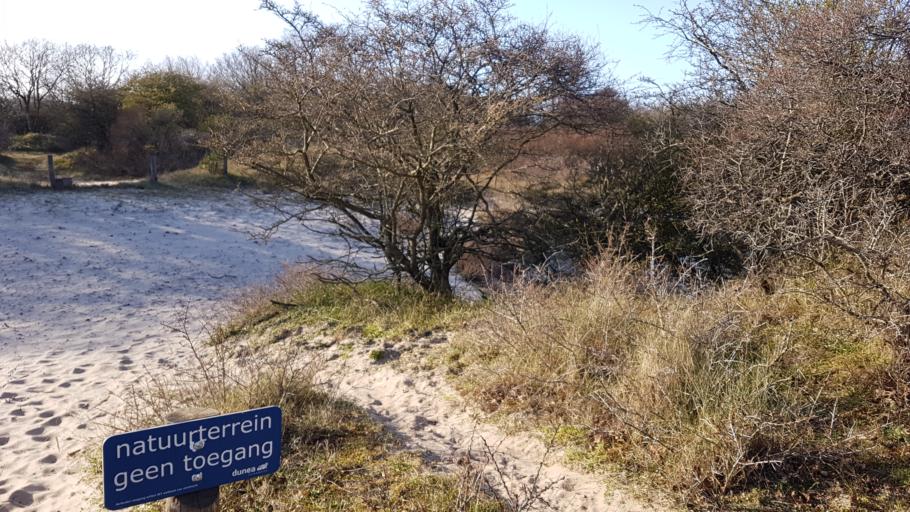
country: NL
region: South Holland
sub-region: Gemeente Wassenaar
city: Wassenaar
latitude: 52.1397
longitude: 4.3415
